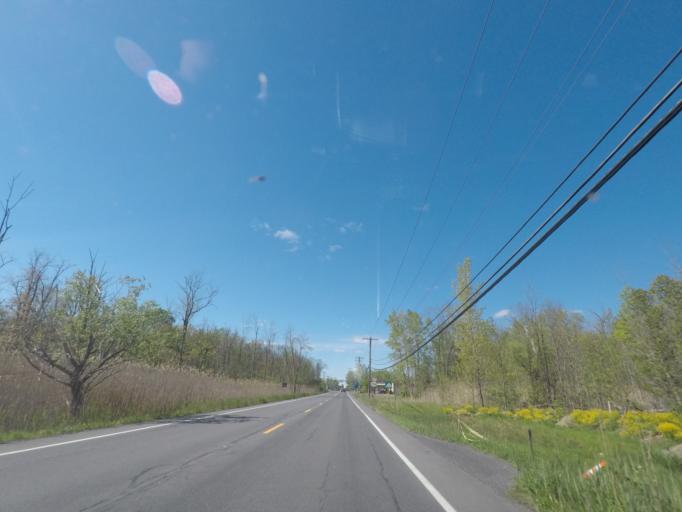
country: US
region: New York
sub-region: Rensselaer County
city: Castleton-on-Hudson
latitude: 42.5463
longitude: -73.8070
